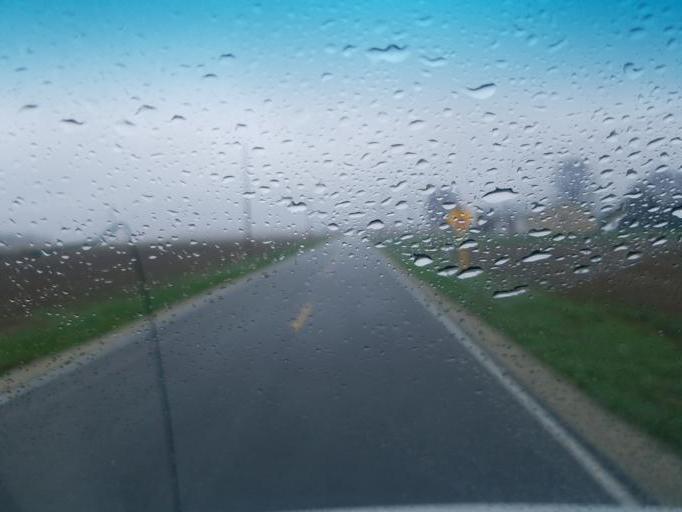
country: US
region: Ohio
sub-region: Wood County
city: North Baltimore
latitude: 41.2171
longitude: -83.6343
